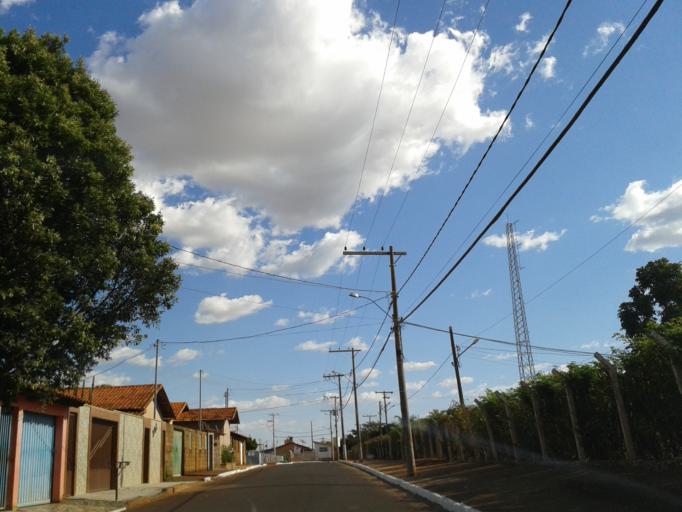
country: BR
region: Minas Gerais
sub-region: Capinopolis
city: Capinopolis
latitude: -18.6944
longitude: -49.5649
